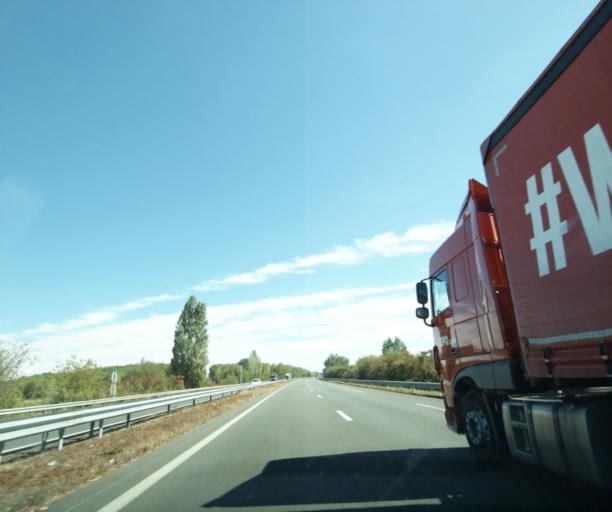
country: FR
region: Aquitaine
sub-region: Departement du Lot-et-Garonne
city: Sainte-Colombe-en-Bruilhois
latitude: 44.2080
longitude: 0.4843
